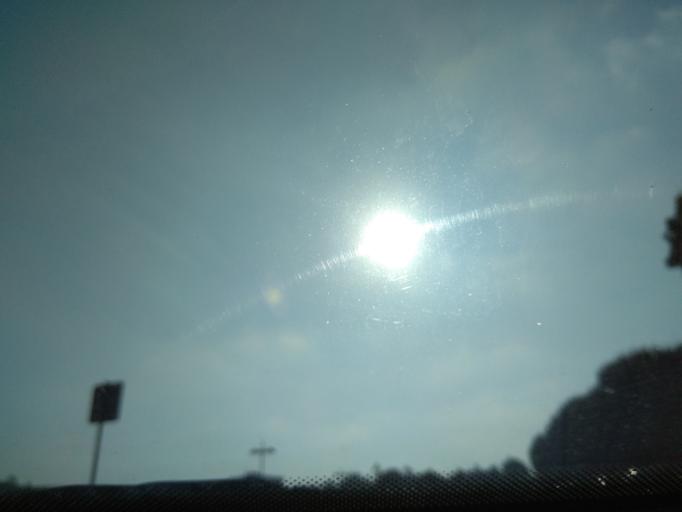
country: PT
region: Porto
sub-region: Maia
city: Anta
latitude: 41.2792
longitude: -8.6035
